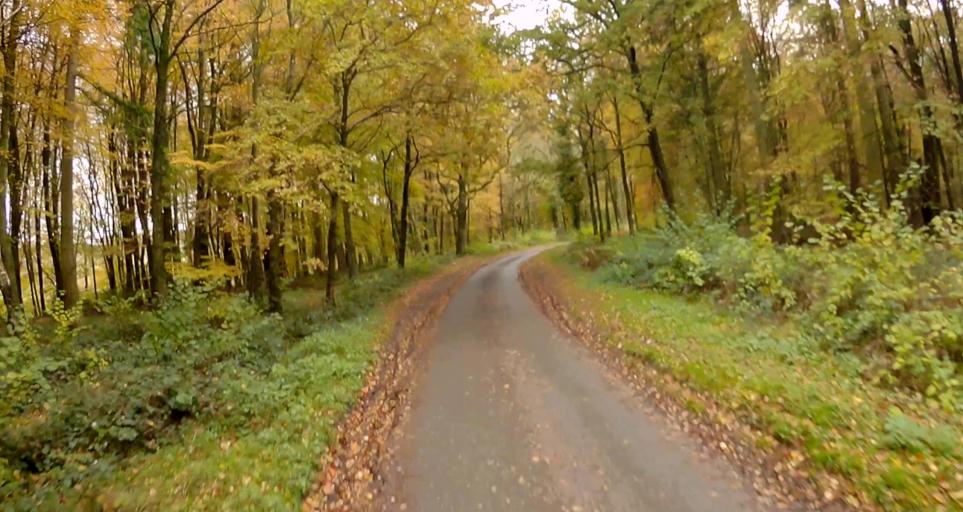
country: GB
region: England
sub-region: Hampshire
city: Long Sutton
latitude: 51.2052
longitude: -0.9489
